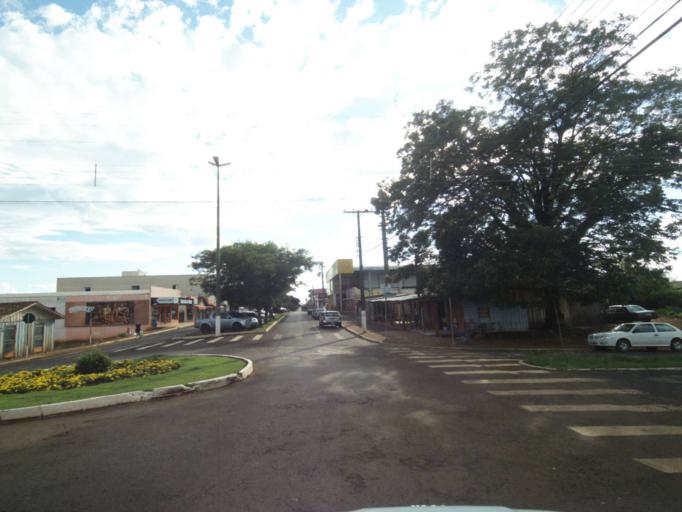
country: BR
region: Parana
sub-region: Laranjeiras Do Sul
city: Laranjeiras do Sul
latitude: -25.4915
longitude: -52.5283
